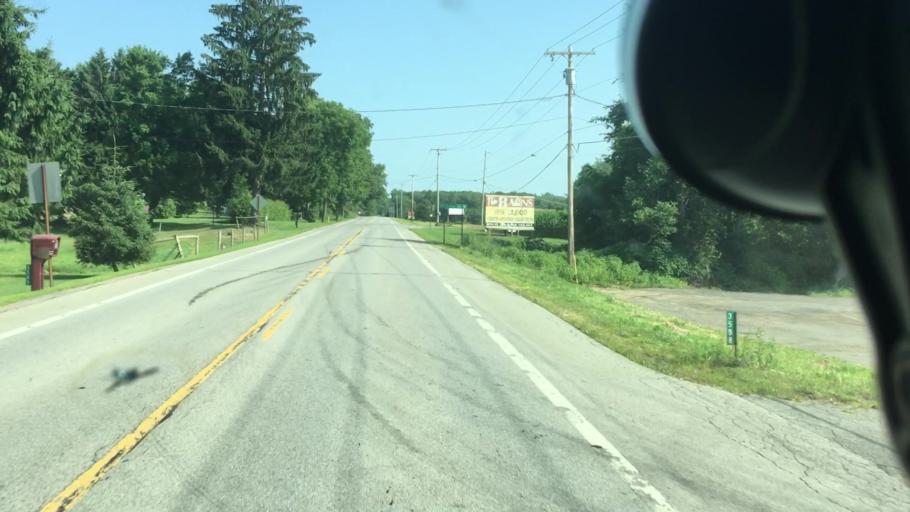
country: US
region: Pennsylvania
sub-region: Butler County
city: Slippery Rock
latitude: 41.0300
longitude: -80.1916
